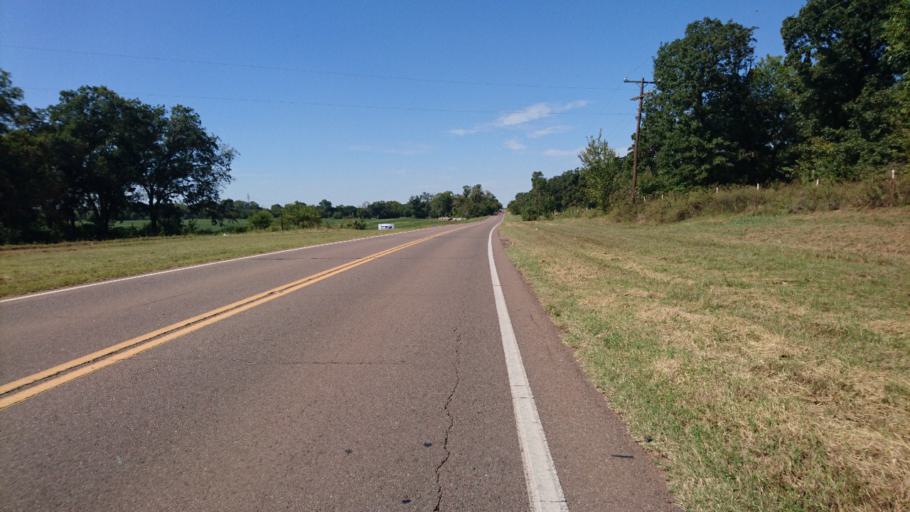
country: US
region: Oklahoma
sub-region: Oklahoma County
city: Luther
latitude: 35.6599
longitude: -97.2766
